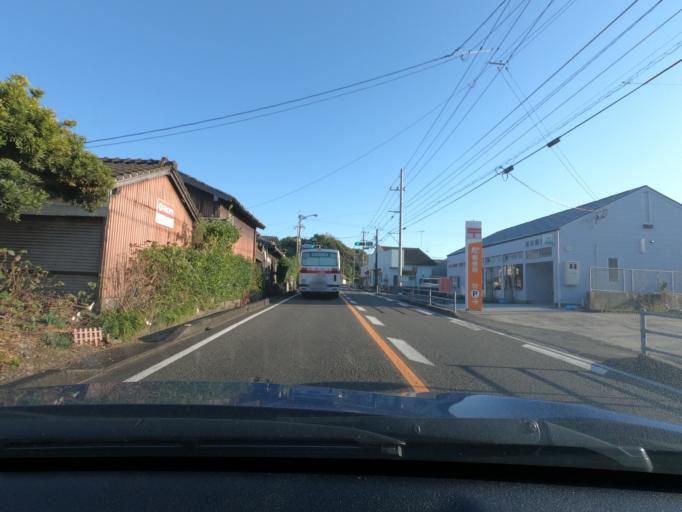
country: JP
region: Kagoshima
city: Akune
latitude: 31.9874
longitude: 130.2030
